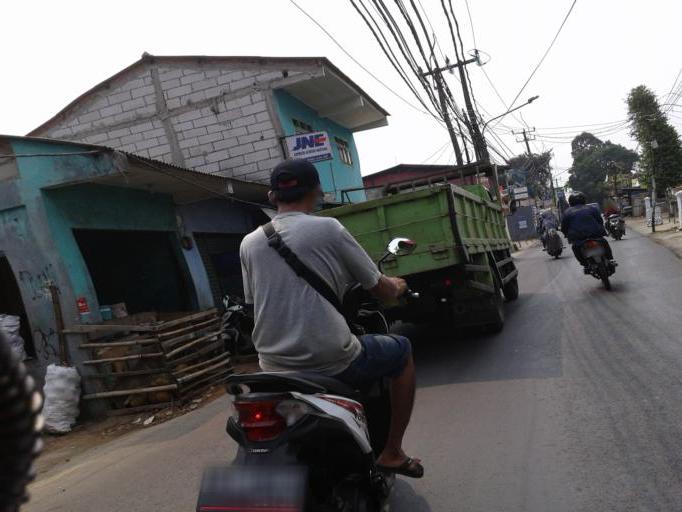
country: ID
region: Banten
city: South Tangerang
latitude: -6.2929
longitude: 106.7421
